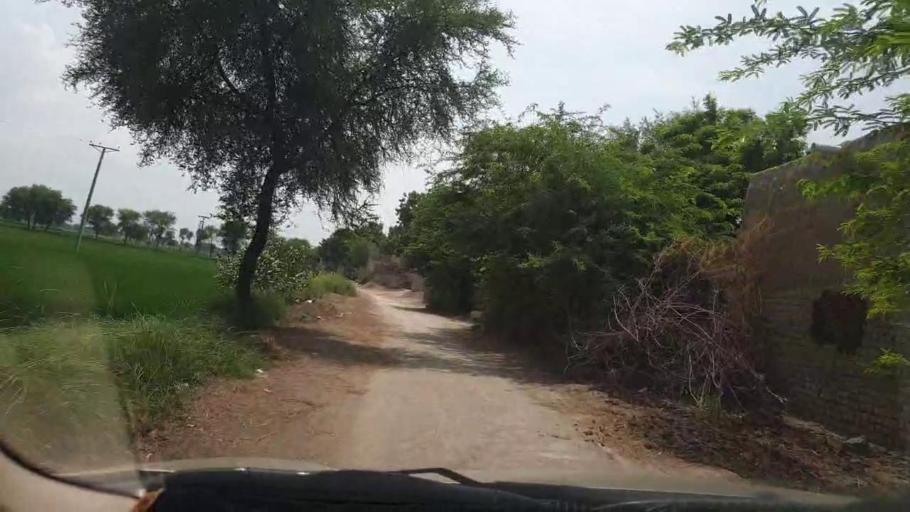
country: PK
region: Sindh
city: Larkana
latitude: 27.5930
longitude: 68.1218
